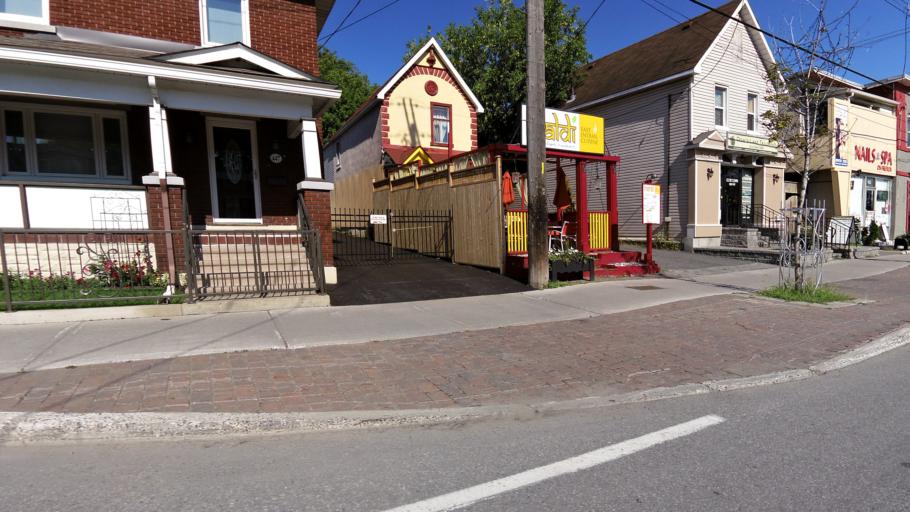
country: CA
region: Ontario
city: Ottawa
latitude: 45.3990
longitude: -75.7085
